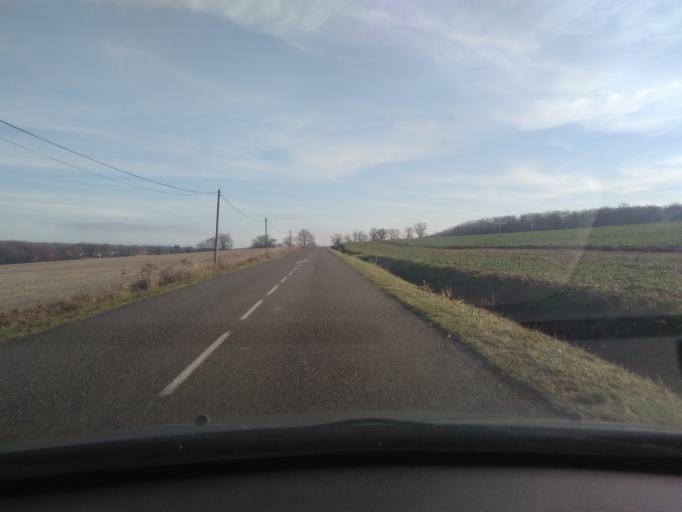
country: FR
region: Bourgogne
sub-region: Departement de la Nievre
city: Saint-Parize-le-Chatel
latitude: 46.8127
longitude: 3.2598
